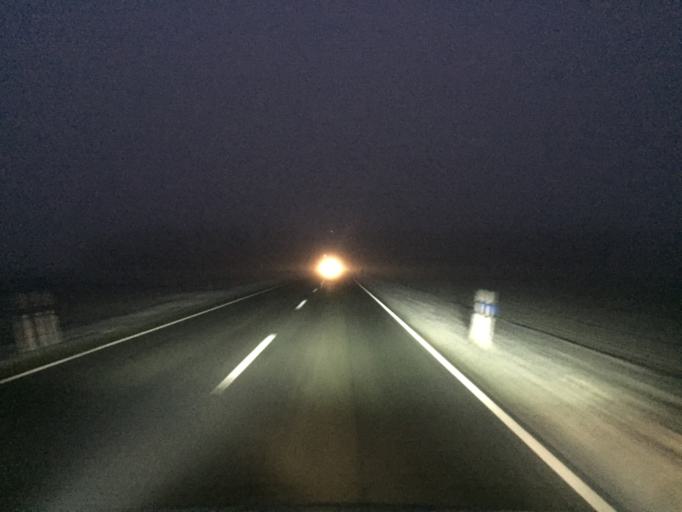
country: DE
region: Lower Saxony
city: Kirchdorf
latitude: 52.6159
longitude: 8.8934
